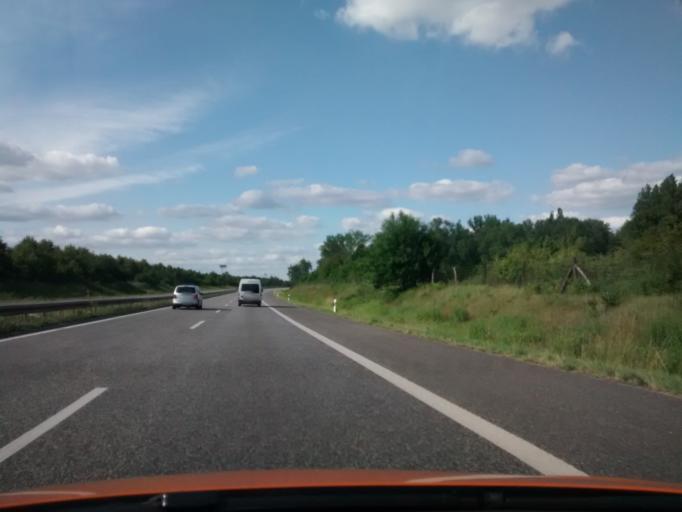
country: DE
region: Brandenburg
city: Grossbeeren
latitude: 52.3616
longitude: 13.2950
